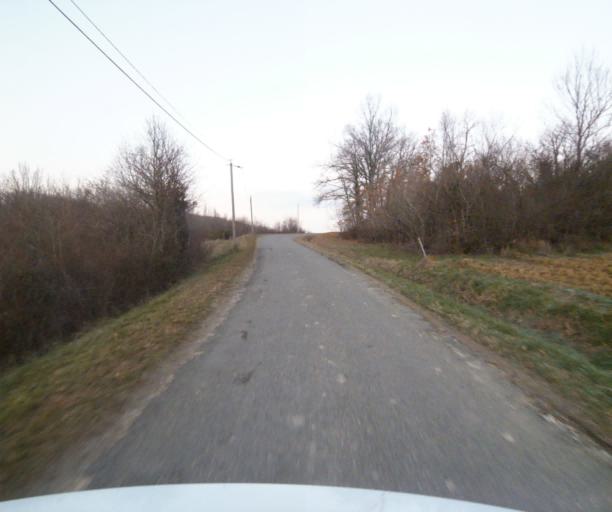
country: FR
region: Midi-Pyrenees
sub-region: Departement du Tarn-et-Garonne
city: Moissac
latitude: 44.1233
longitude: 1.0483
